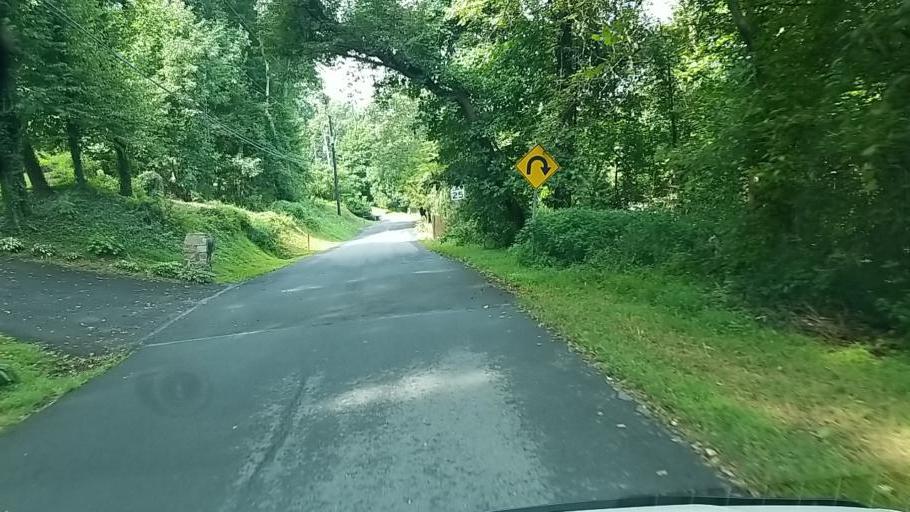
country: US
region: Pennsylvania
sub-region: Dauphin County
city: Millersburg
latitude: 40.5269
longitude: -76.9611
